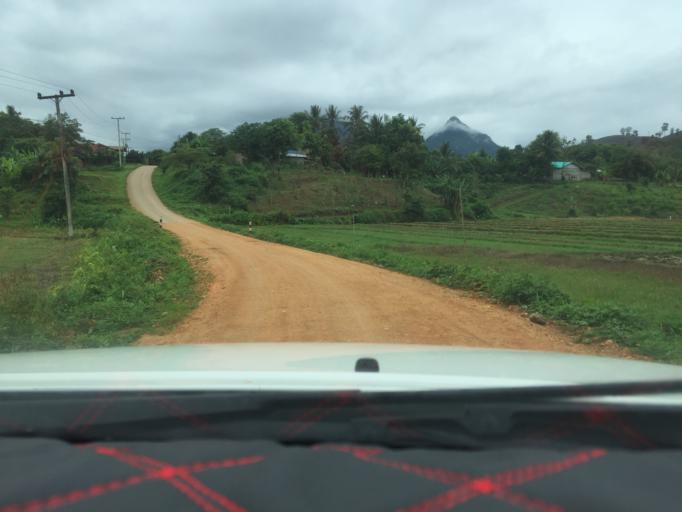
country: TH
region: Phayao
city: Phu Sang
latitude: 19.7723
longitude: 100.5271
